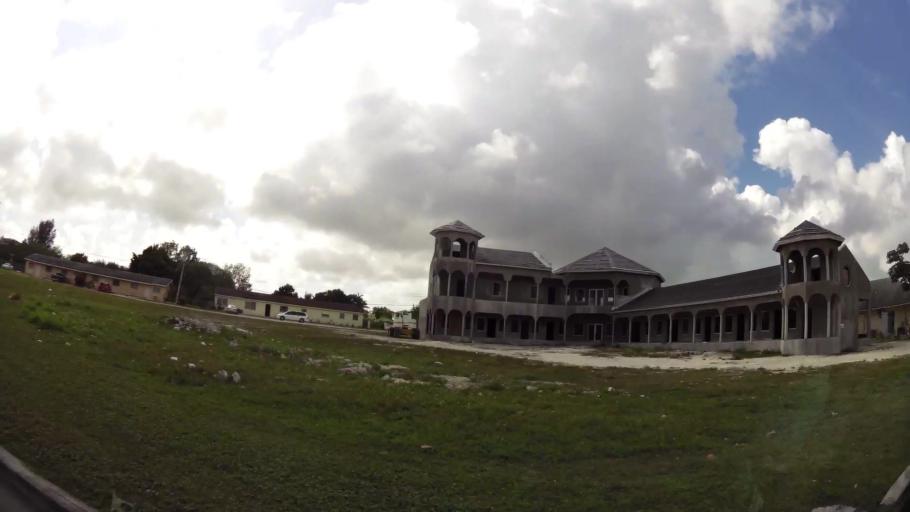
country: BS
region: Freeport
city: Freeport
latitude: 26.5309
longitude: -78.6986
